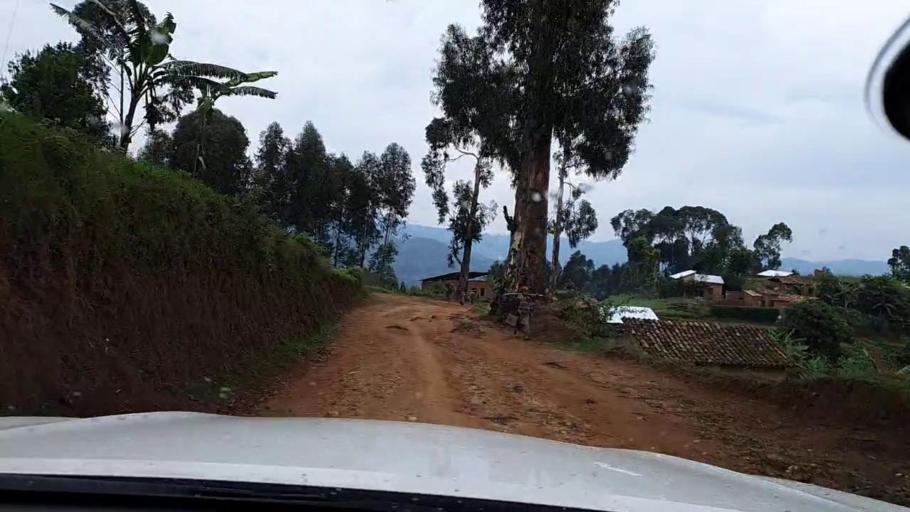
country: RW
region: Southern Province
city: Nzega
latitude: -2.3803
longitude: 29.2422
